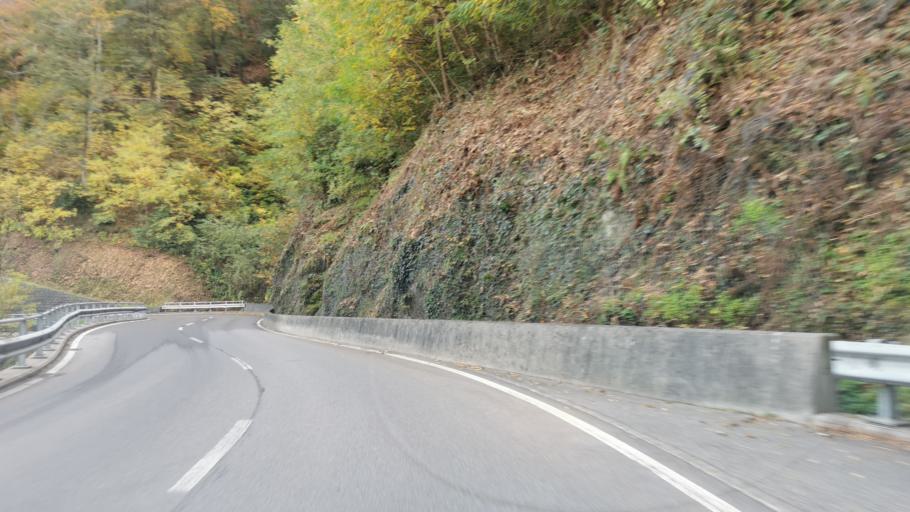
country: CH
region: Ticino
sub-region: Lugano District
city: Pura
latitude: 45.9973
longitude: 8.8597
